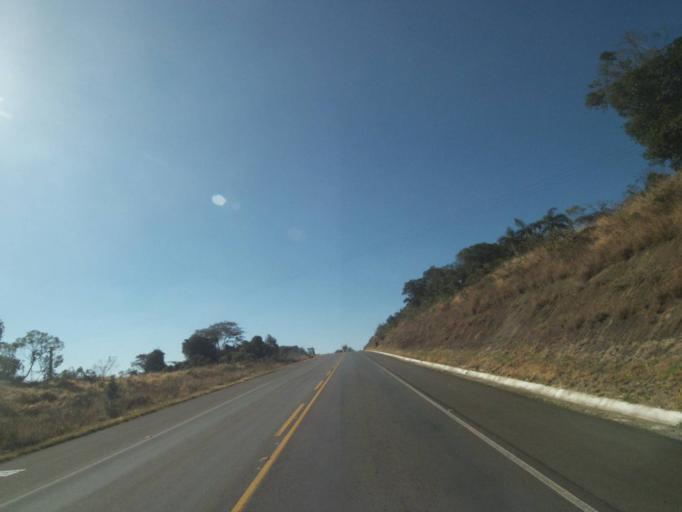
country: BR
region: Parana
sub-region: Tibagi
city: Tibagi
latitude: -24.7843
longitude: -50.4687
